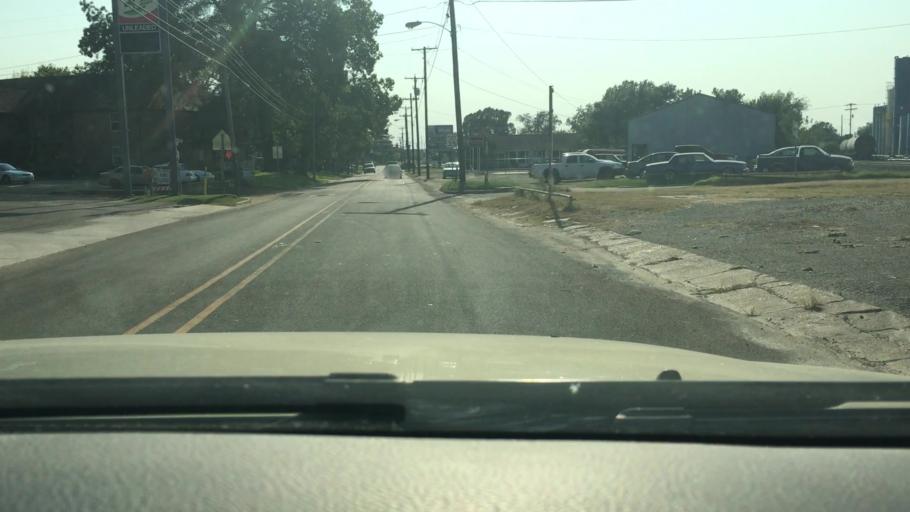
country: US
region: Texas
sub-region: Hopkins County
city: Sulphur Springs
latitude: 33.1350
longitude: -95.6107
